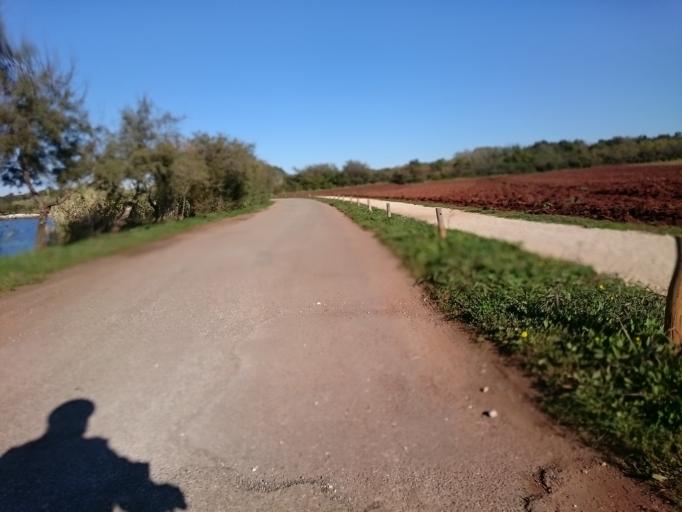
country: HR
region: Istarska
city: Novigrad
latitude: 45.3341
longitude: 13.5443
